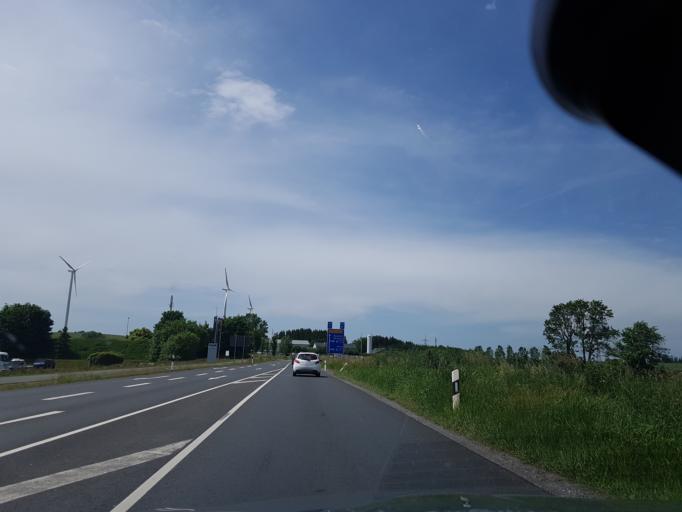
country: DE
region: Bavaria
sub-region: Upper Franconia
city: Munchberg
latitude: 50.2031
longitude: 11.7818
